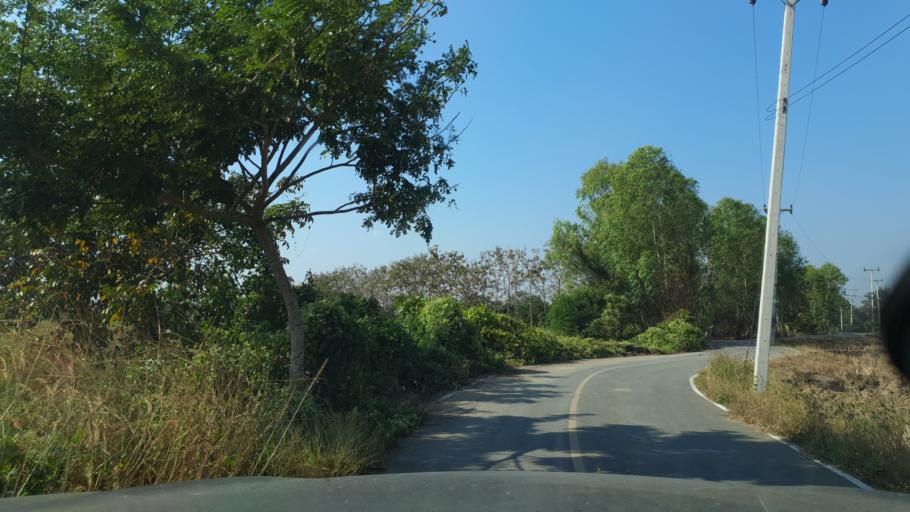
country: TH
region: Lamphun
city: Ban Thi
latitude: 18.6879
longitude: 99.0940
